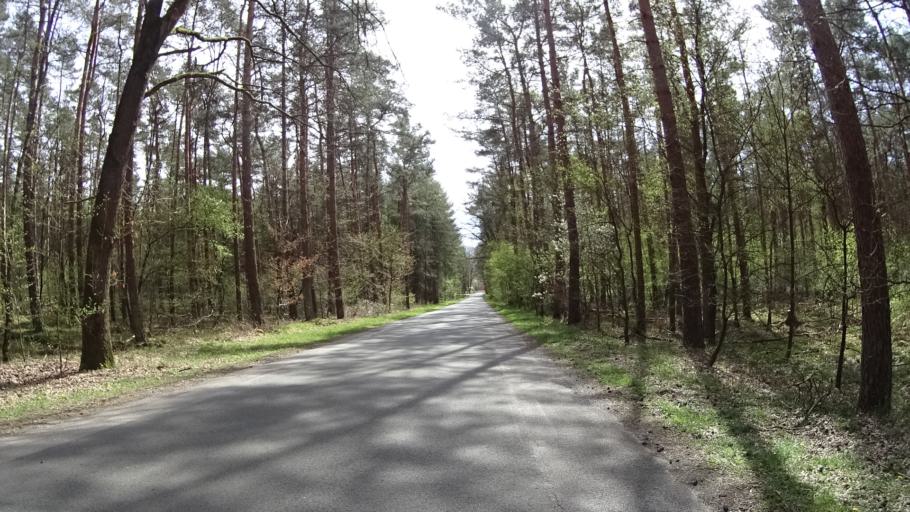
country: DE
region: Lower Saxony
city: Emsburen
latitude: 52.4351
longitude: 7.3499
